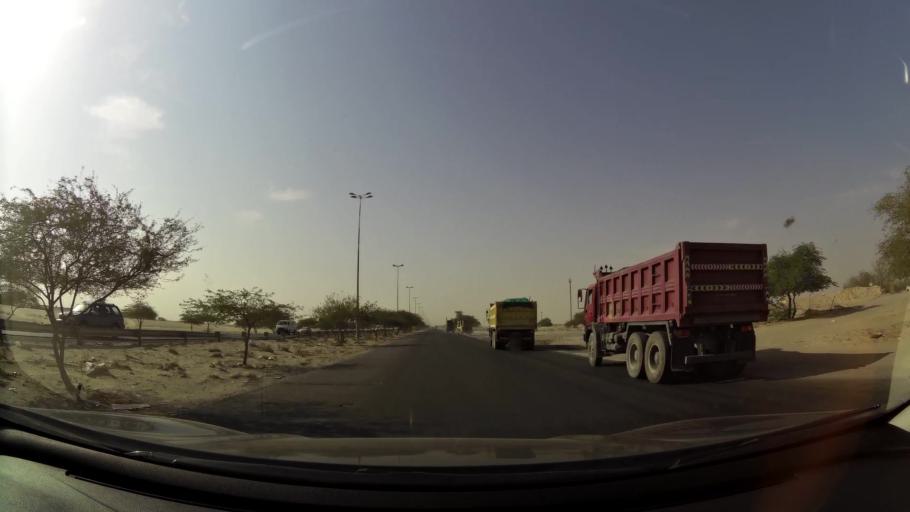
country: KW
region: Al Ahmadi
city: Al Ahmadi
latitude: 28.9387
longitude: 48.1112
